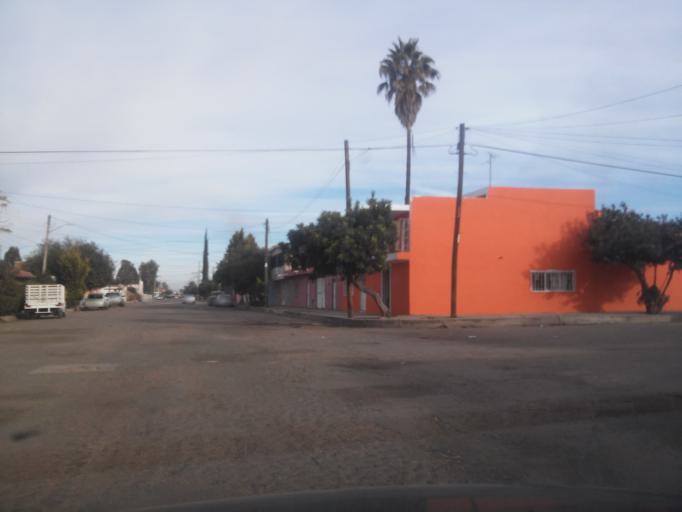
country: MX
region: Durango
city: Victoria de Durango
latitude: 24.0247
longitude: -104.6362
